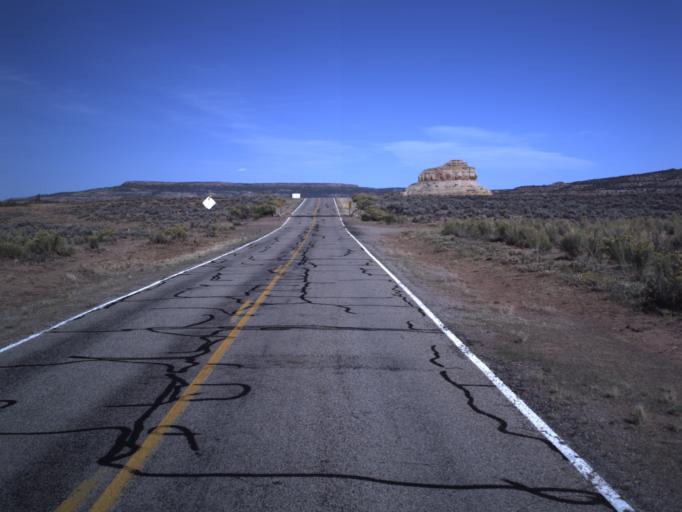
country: US
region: Utah
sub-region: San Juan County
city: Monticello
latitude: 38.0721
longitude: -109.3583
